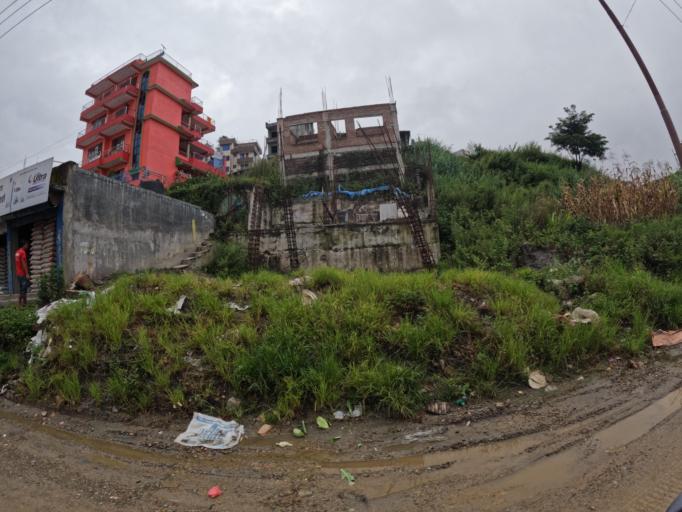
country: NP
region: Central Region
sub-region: Bagmati Zone
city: Kathmandu
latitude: 27.7608
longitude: 85.3190
